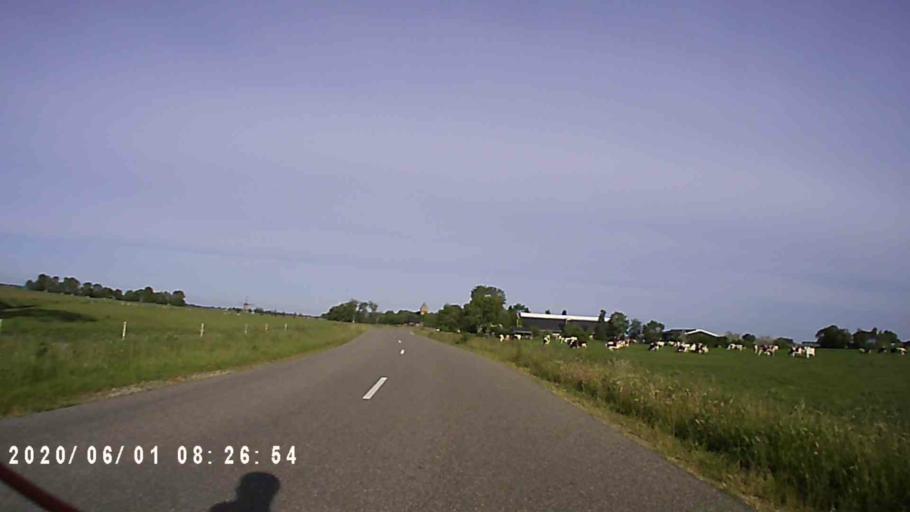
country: NL
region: Friesland
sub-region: Gemeente Ferwerderadiel
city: Burdaard
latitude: 53.2997
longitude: 5.8591
